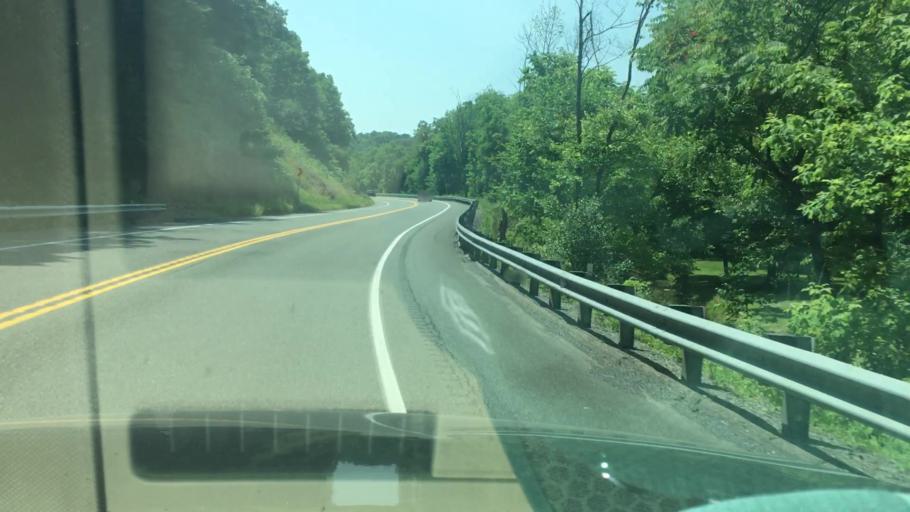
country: US
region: Pennsylvania
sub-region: Lehigh County
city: Schnecksville
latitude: 40.6687
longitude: -75.6860
